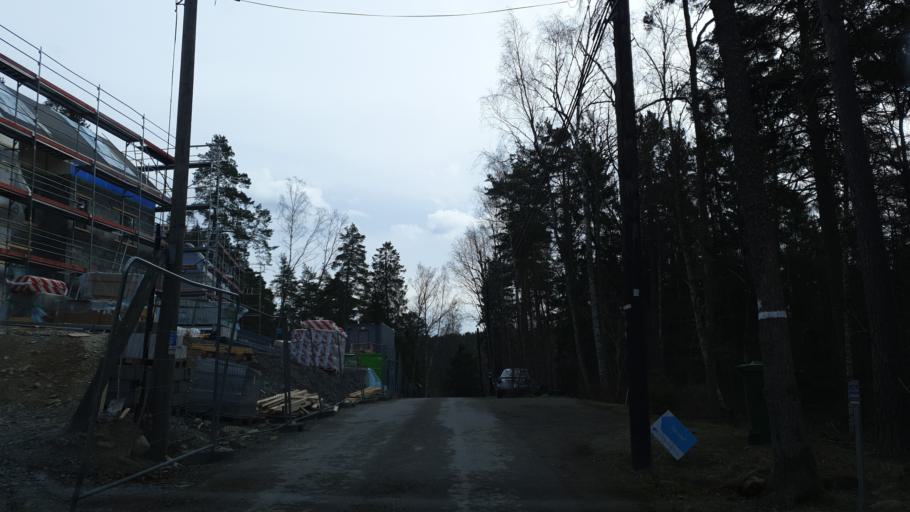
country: SE
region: Stockholm
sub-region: Nacka Kommun
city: Boo
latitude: 59.3316
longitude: 18.2910
